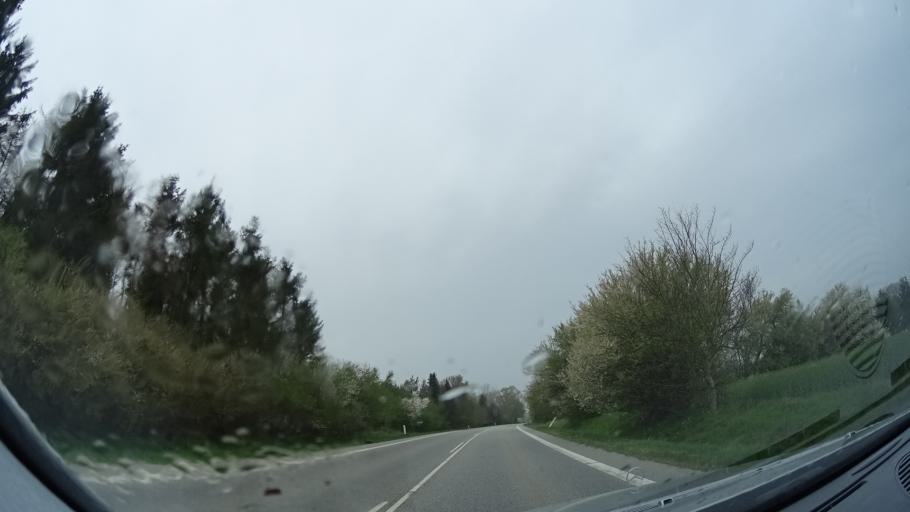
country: DK
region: Zealand
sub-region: Holbaek Kommune
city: Vipperod
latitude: 55.6919
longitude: 11.7891
